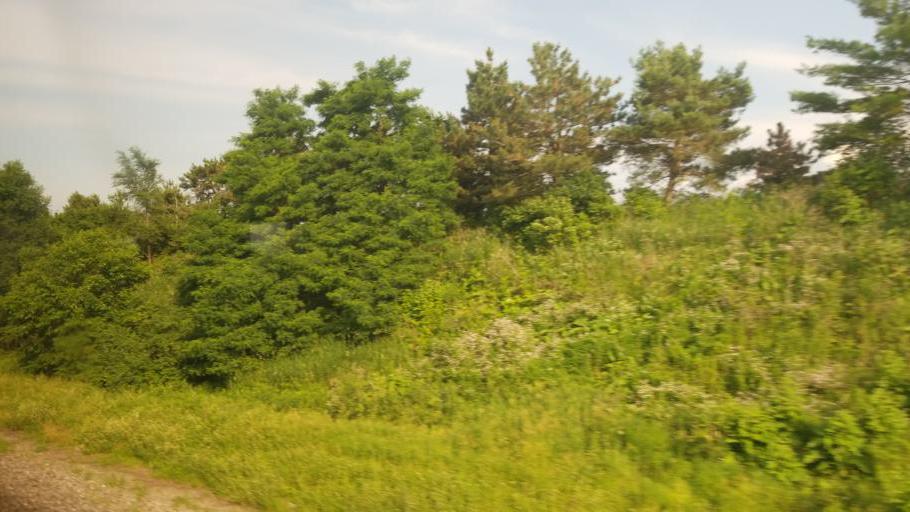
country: US
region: Illinois
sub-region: Kendall County
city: Lynwood
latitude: 41.6967
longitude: -88.3845
